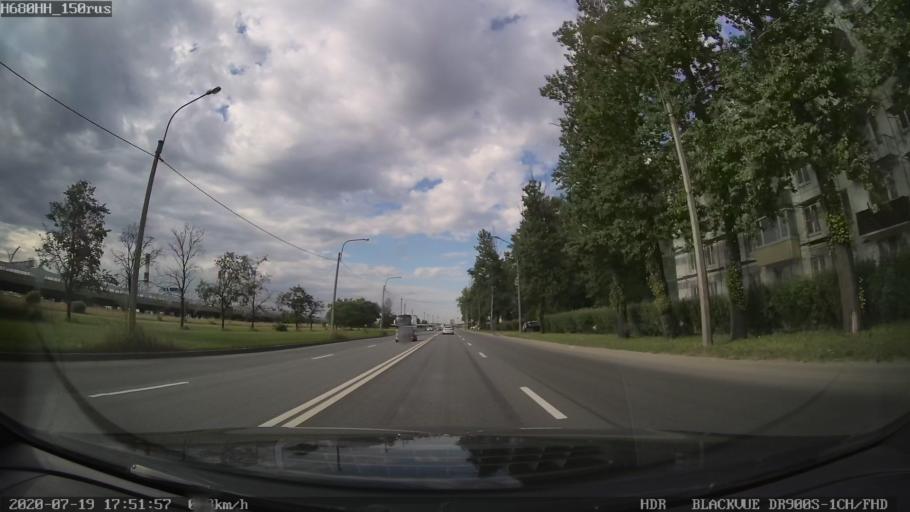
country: RU
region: St.-Petersburg
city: Avtovo
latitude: 59.8620
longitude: 30.2946
